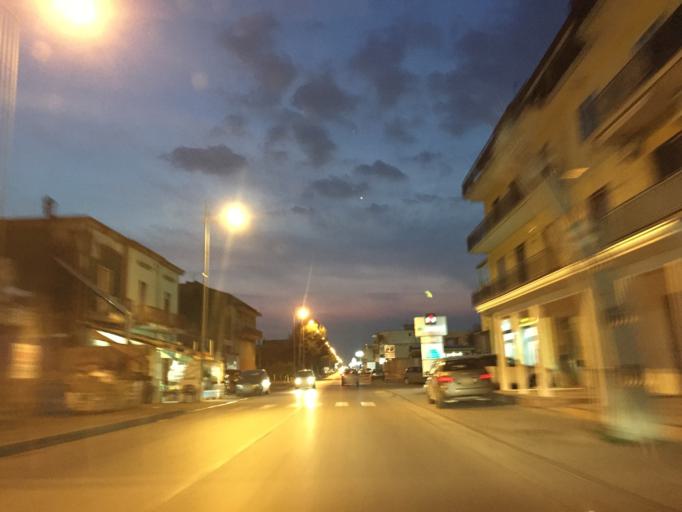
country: IT
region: Campania
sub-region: Provincia di Salerno
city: San Lorenzo
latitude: 40.7480
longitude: 14.5936
